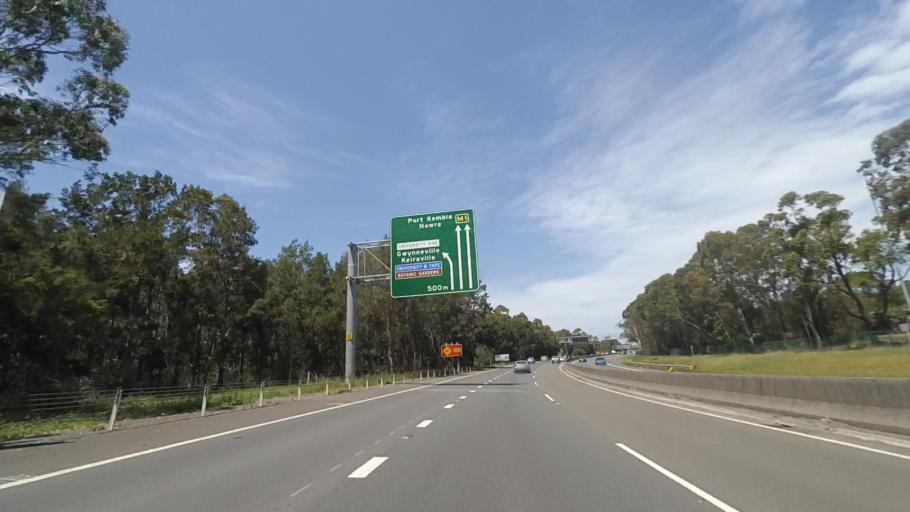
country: AU
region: New South Wales
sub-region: Wollongong
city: Mount Ousley
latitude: -34.4044
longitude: 150.8837
